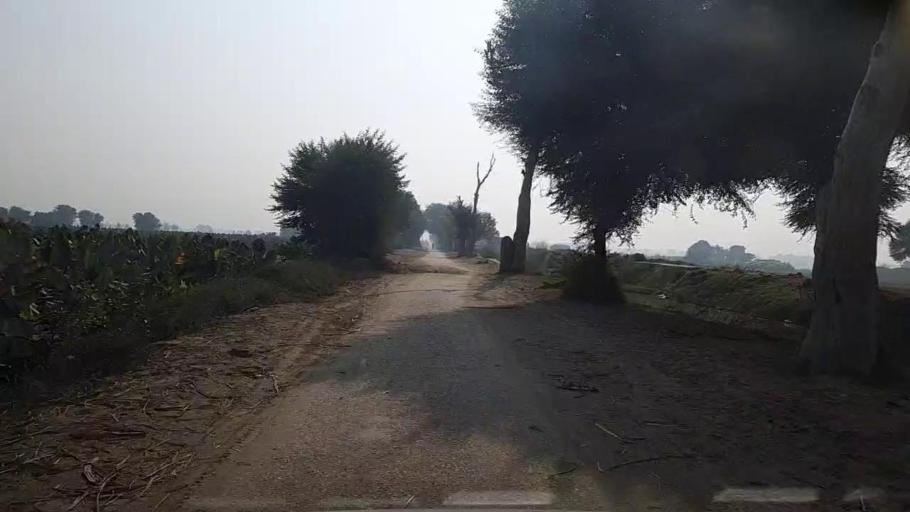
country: PK
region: Sindh
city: Setharja Old
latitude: 27.1119
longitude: 68.5090
